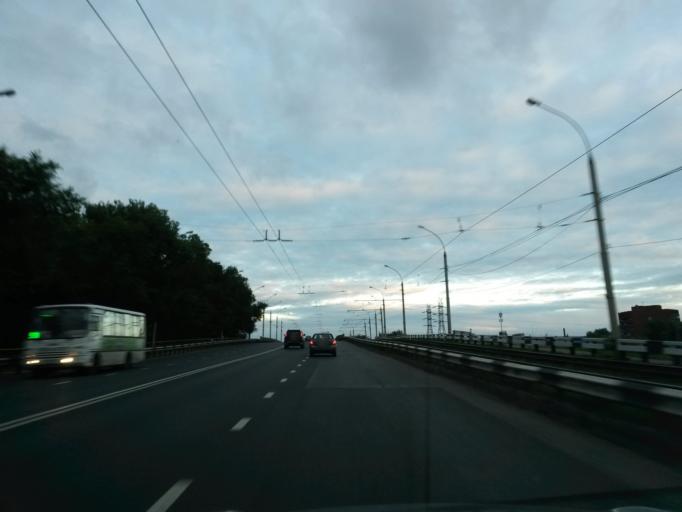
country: RU
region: Jaroslavl
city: Yaroslavl
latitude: 57.6451
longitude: 39.8523
